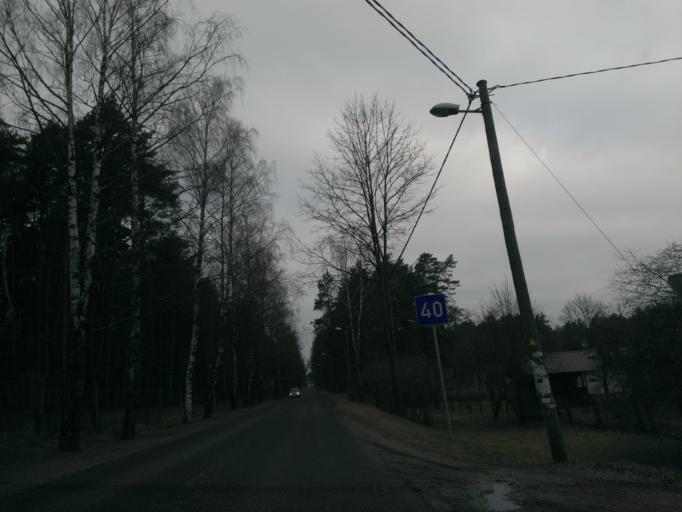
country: LV
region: Riga
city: Bergi
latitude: 56.9920
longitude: 24.2884
